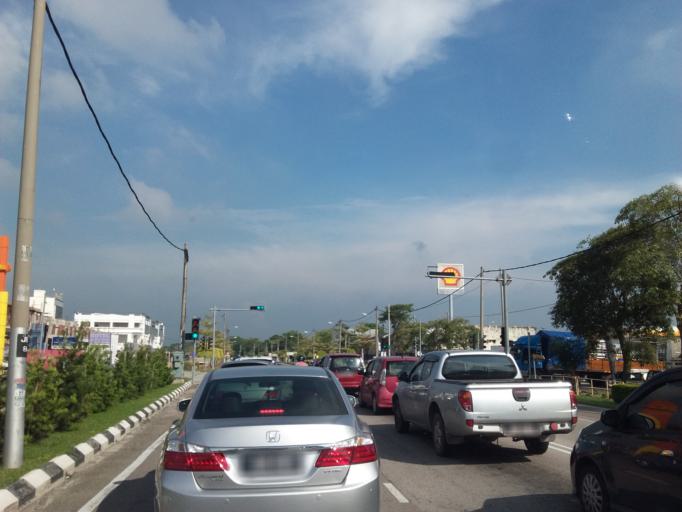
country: MY
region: Johor
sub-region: Daerah Batu Pahat
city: Batu Pahat
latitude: 1.8589
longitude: 102.9310
